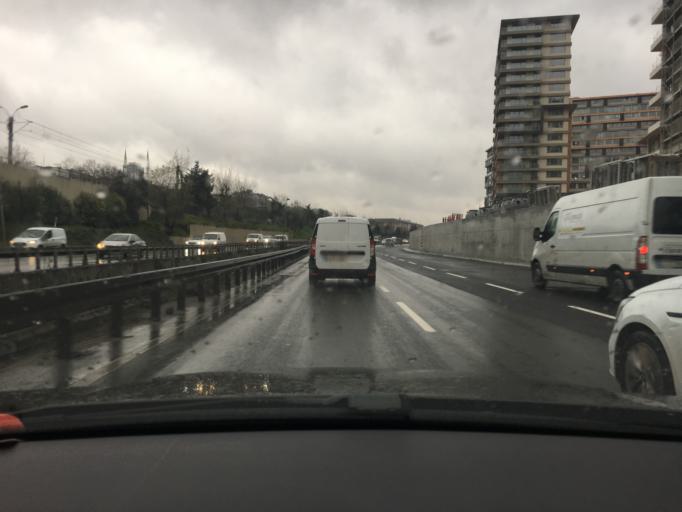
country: TR
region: Istanbul
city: merter keresteciler
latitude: 41.0227
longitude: 28.9001
